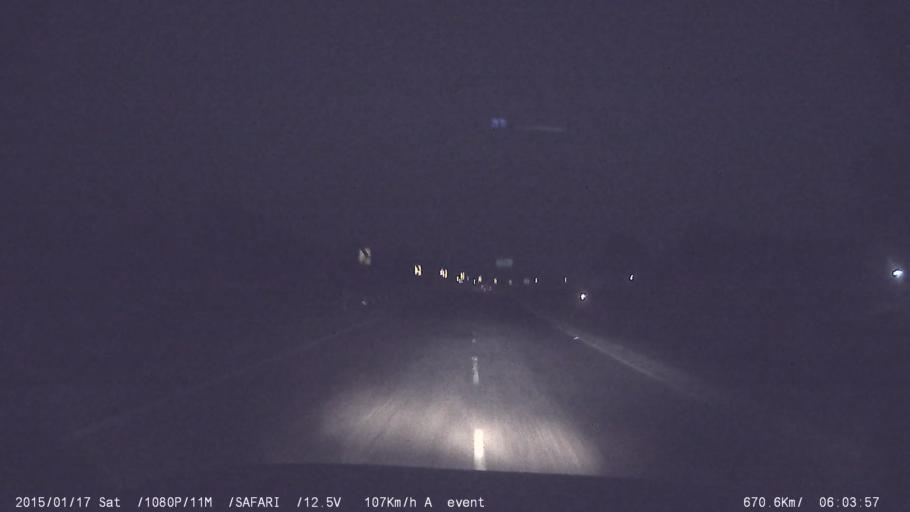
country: IN
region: Tamil Nadu
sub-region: Kancheepuram
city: Kanchipuram
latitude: 12.8781
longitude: 79.6108
